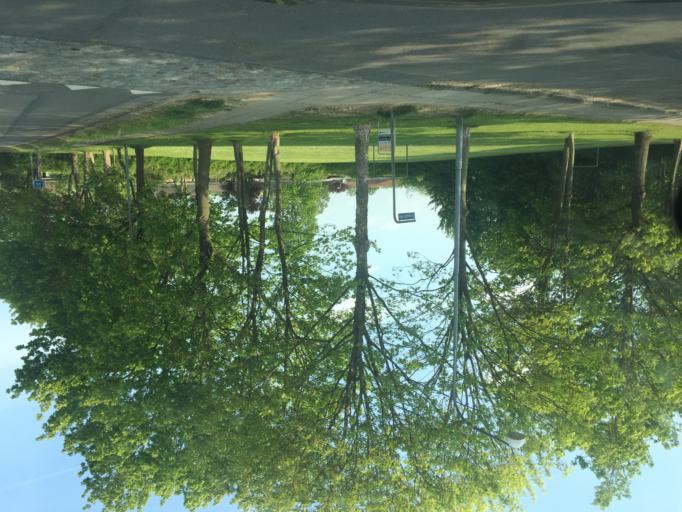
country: DK
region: South Denmark
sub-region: Odense Kommune
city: Bellinge
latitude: 55.3524
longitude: 10.3507
